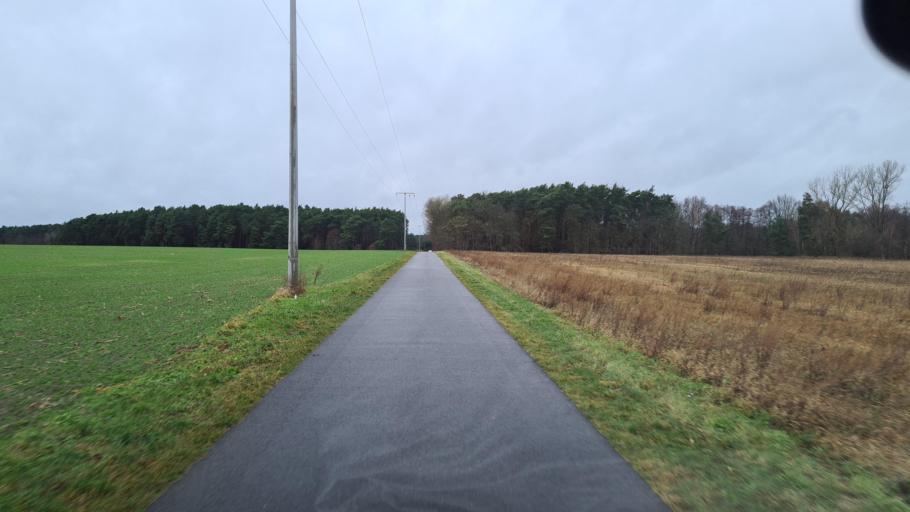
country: DE
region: Brandenburg
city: Tauche
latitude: 52.0870
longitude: 14.1473
